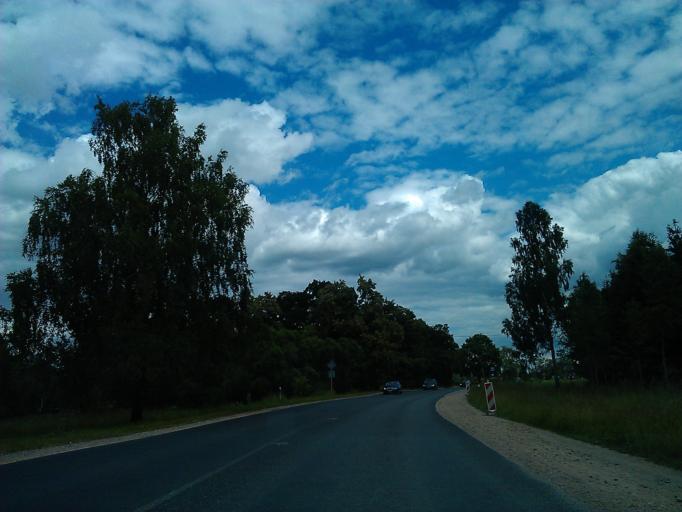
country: LV
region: Jelgava
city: Jelgava
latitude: 56.6508
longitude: 23.6288
